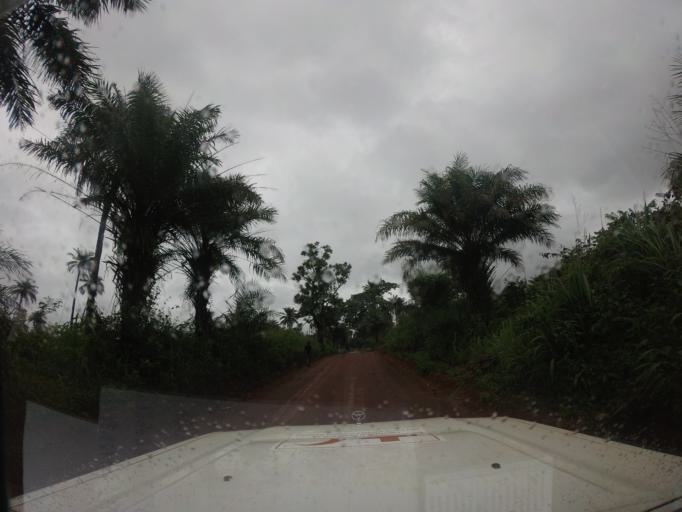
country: SL
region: Northern Province
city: Kambia
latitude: 9.1350
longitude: -12.8820
